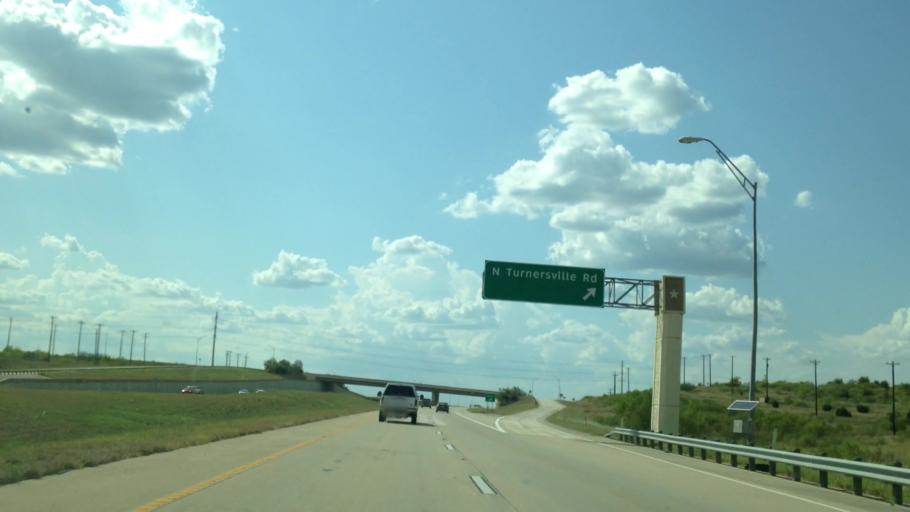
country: US
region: Texas
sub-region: Travis County
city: Onion Creek
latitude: 30.1002
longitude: -97.7774
